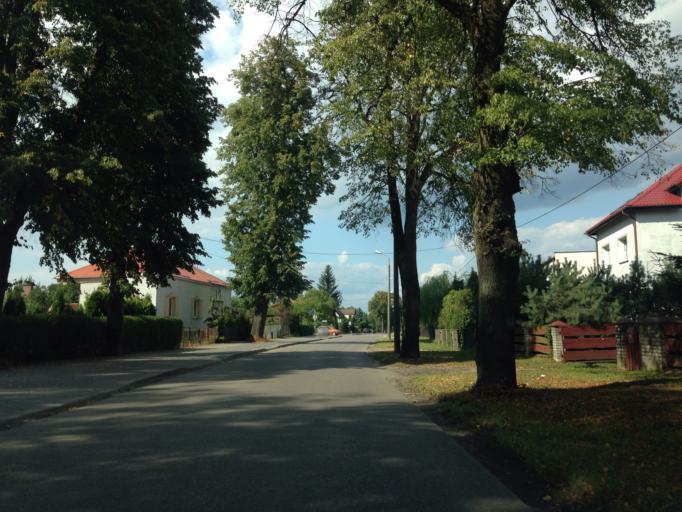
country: PL
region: Warmian-Masurian Voivodeship
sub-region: Powiat ilawski
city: Ilawa
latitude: 53.6158
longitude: 19.5680
